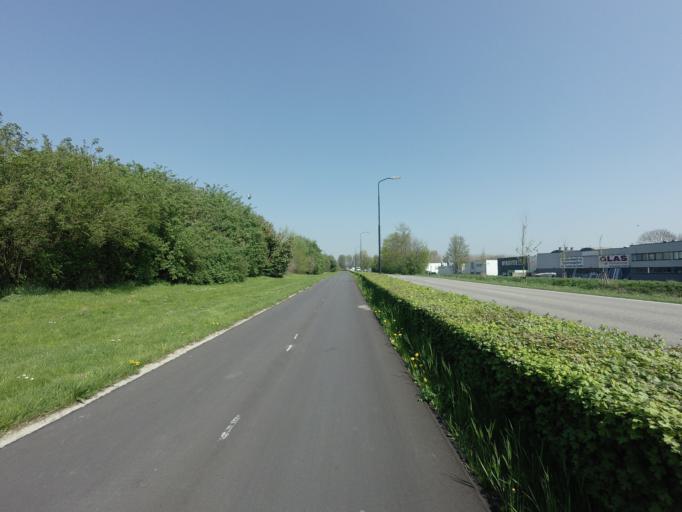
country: NL
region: Utrecht
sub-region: Gemeente De Ronde Venen
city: Mijdrecht
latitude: 52.2099
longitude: 4.8695
